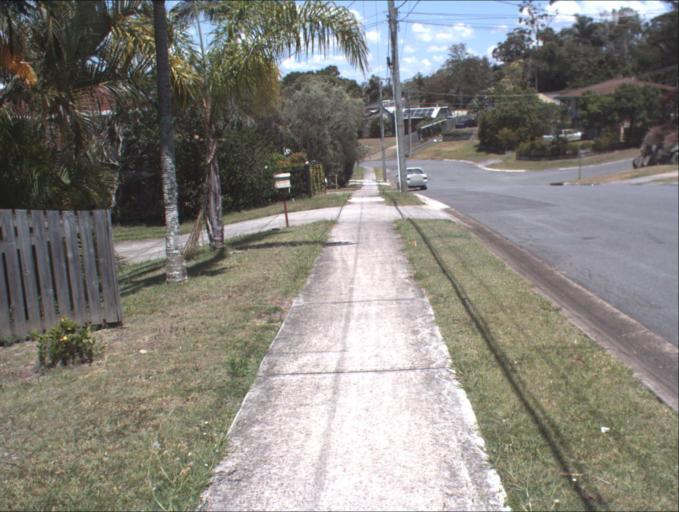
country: AU
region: Queensland
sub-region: Logan
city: Rochedale South
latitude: -27.5988
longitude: 153.1399
